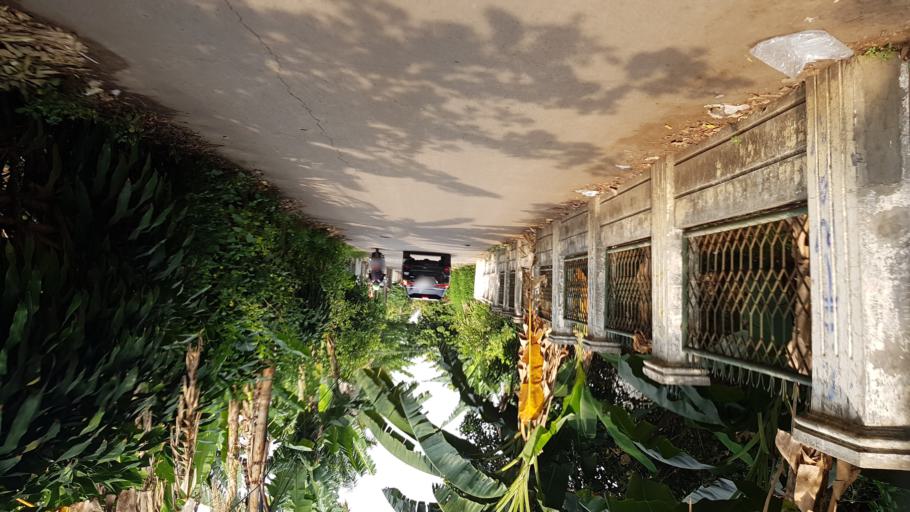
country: ID
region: West Java
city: Pamulang
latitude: -6.3255
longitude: 106.7966
